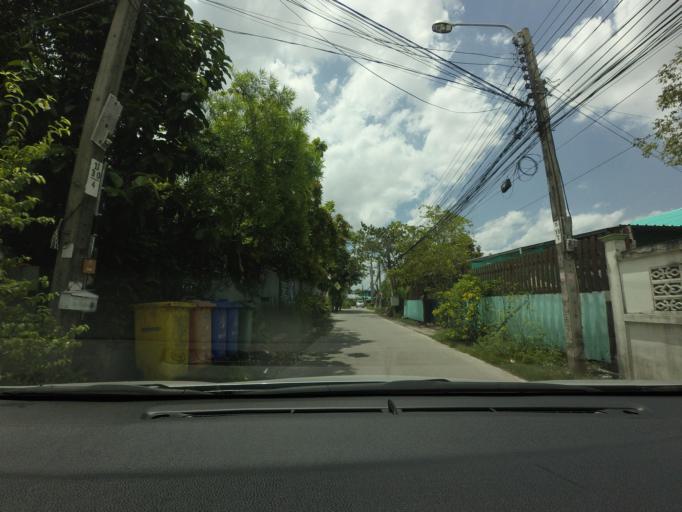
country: TH
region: Samut Prakan
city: Phra Samut Chedi
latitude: 13.6238
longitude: 100.5694
